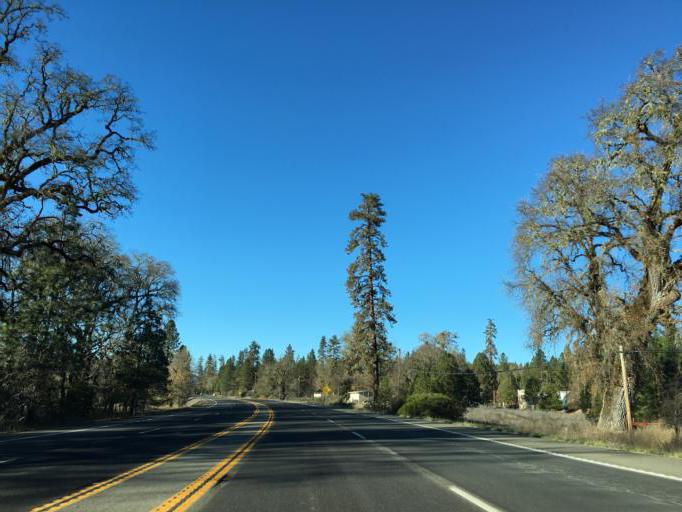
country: US
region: California
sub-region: Mendocino County
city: Laytonville
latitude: 39.7279
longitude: -123.5053
